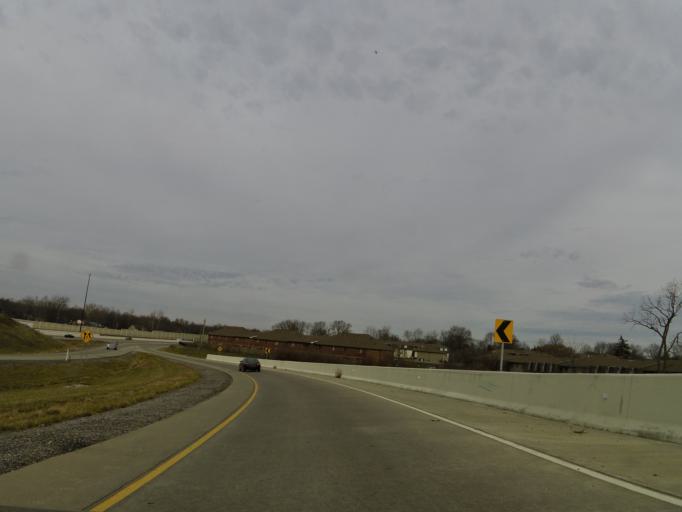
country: US
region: Indiana
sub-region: Marion County
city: Speedway
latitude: 39.8054
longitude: -86.2733
